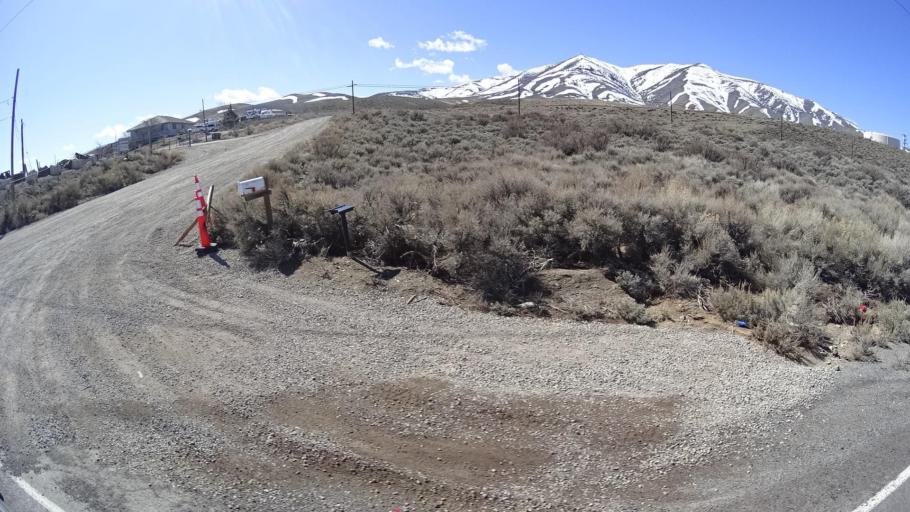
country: US
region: Nevada
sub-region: Washoe County
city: Lemmon Valley
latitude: 39.6197
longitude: -119.8918
